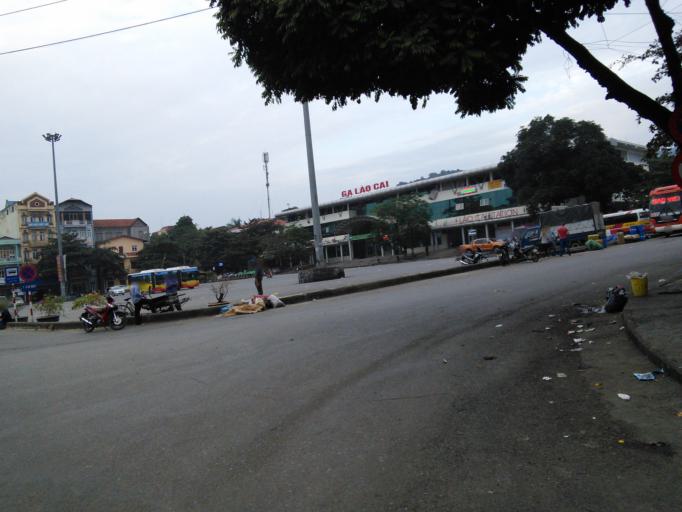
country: VN
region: Lao Cai
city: Lao Cai
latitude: 22.4913
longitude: 103.9779
